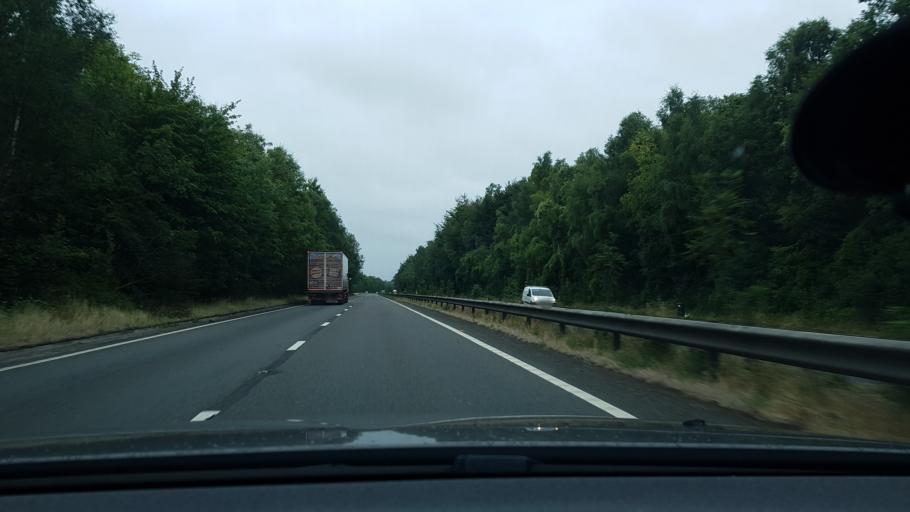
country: GB
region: England
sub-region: Hampshire
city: Highclere
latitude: 51.2686
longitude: -1.3414
